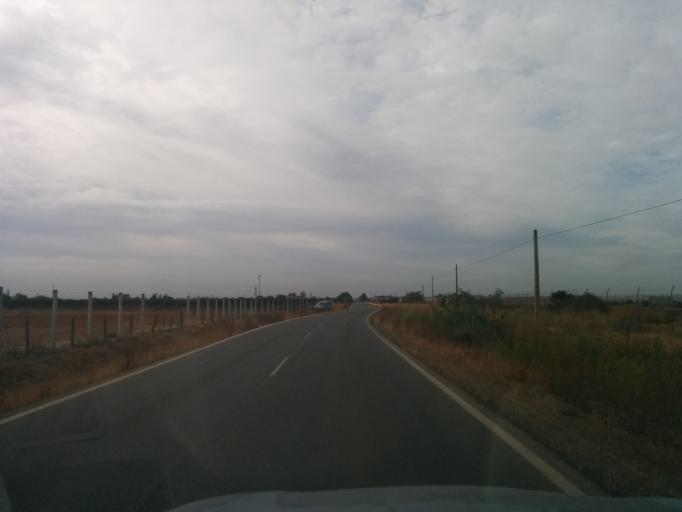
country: ES
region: Andalusia
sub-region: Provincia de Sevilla
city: Guillena
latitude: 37.5241
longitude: -6.0317
